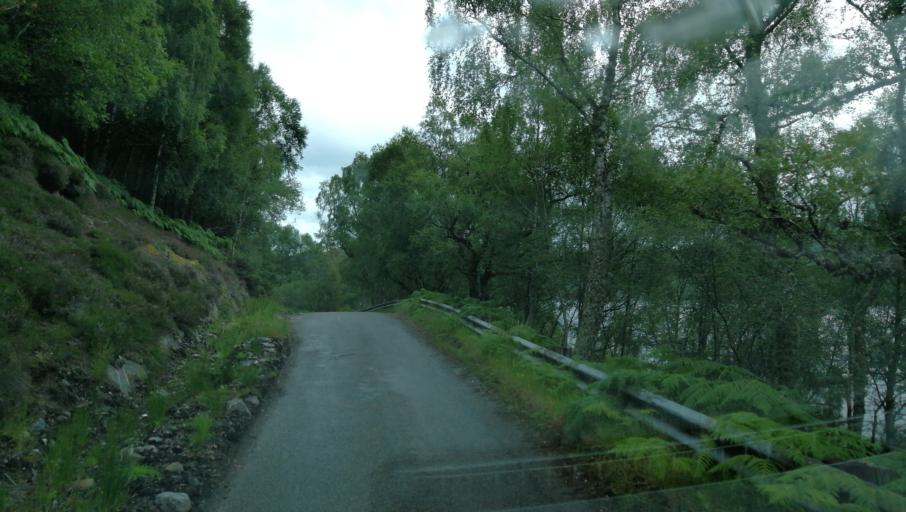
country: GB
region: Scotland
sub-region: Highland
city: Spean Bridge
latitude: 57.2757
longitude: -4.9512
